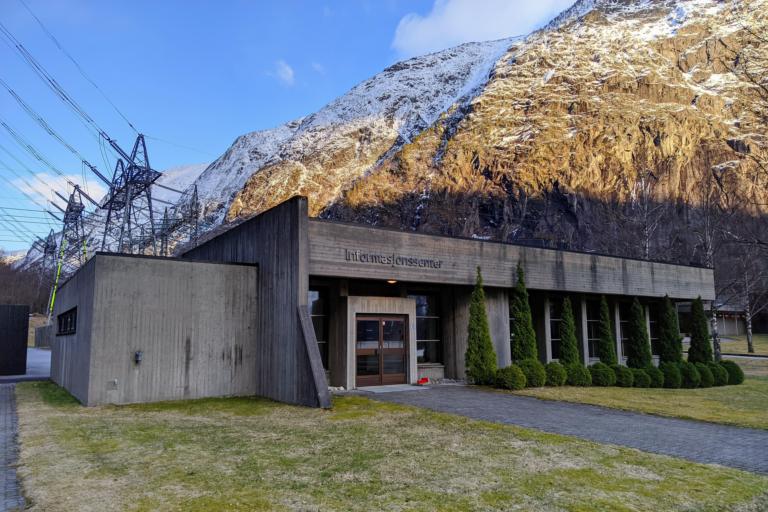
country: NO
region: Hordaland
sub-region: Eidfjord
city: Eidfjord
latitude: 60.4997
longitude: 7.1421
